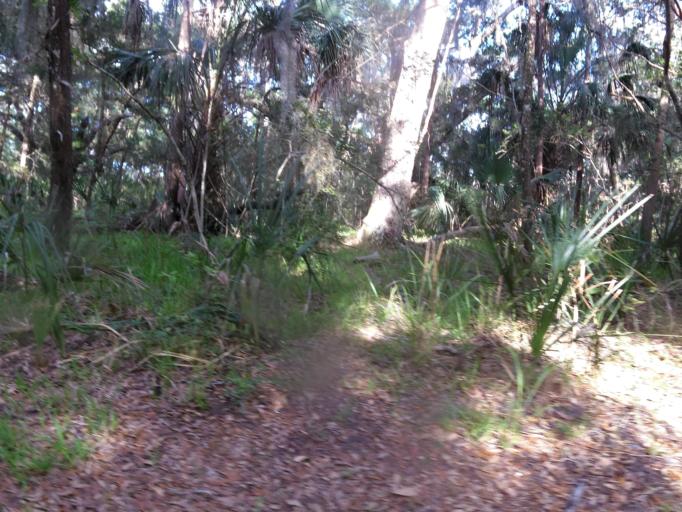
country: US
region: Florida
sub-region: Saint Johns County
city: Villano Beach
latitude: 30.0229
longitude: -81.3448
